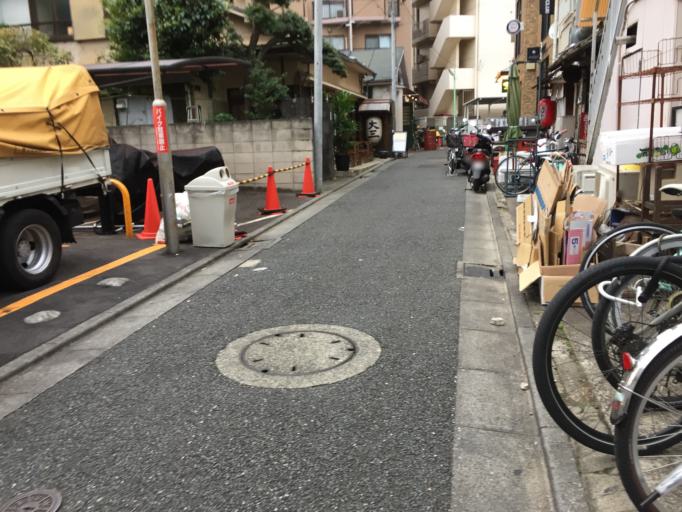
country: JP
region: Tokyo
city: Tokyo
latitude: 35.6426
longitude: 139.6683
